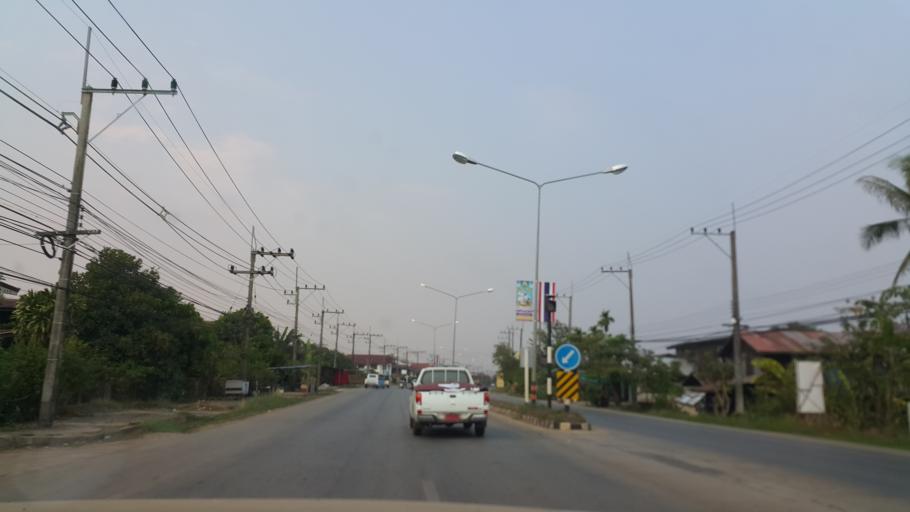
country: TH
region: Nakhon Phanom
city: That Phanom
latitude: 16.9708
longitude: 104.7273
